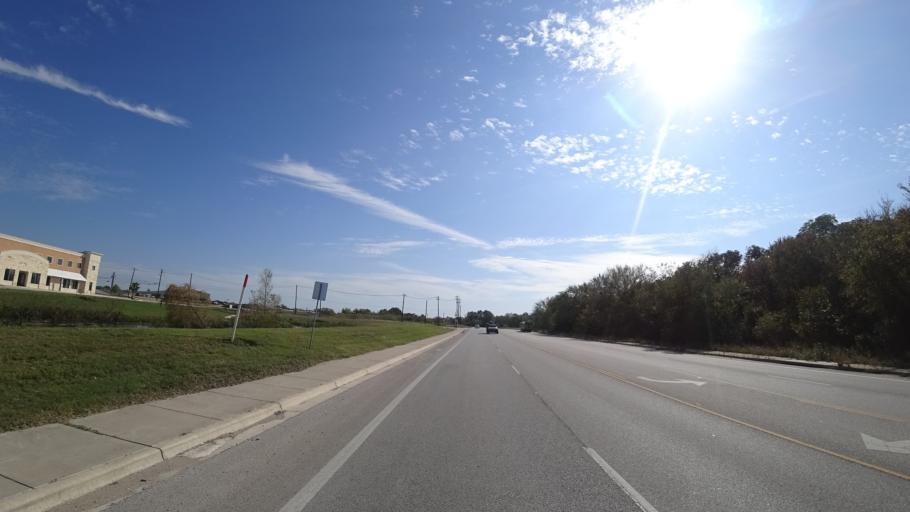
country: US
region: Texas
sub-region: Travis County
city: Pflugerville
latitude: 30.4002
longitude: -97.6334
